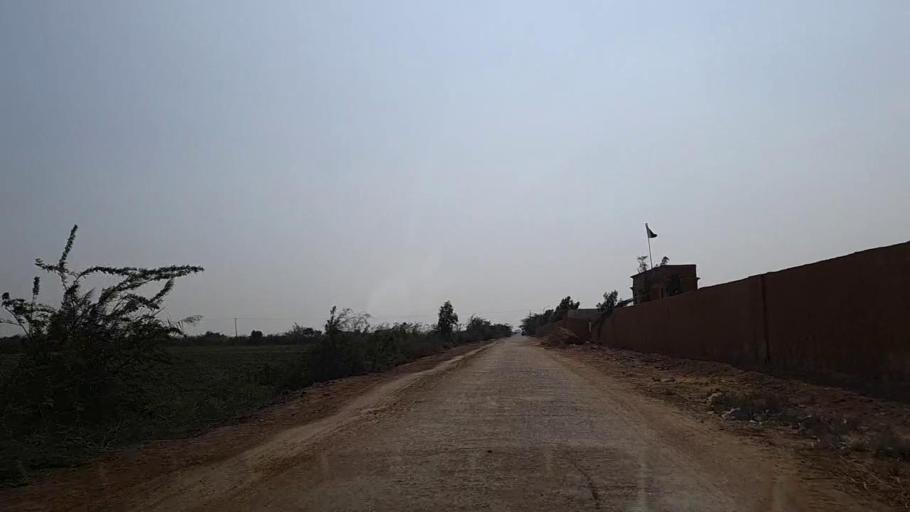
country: PK
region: Sindh
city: Thatta
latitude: 24.7077
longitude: 67.7673
